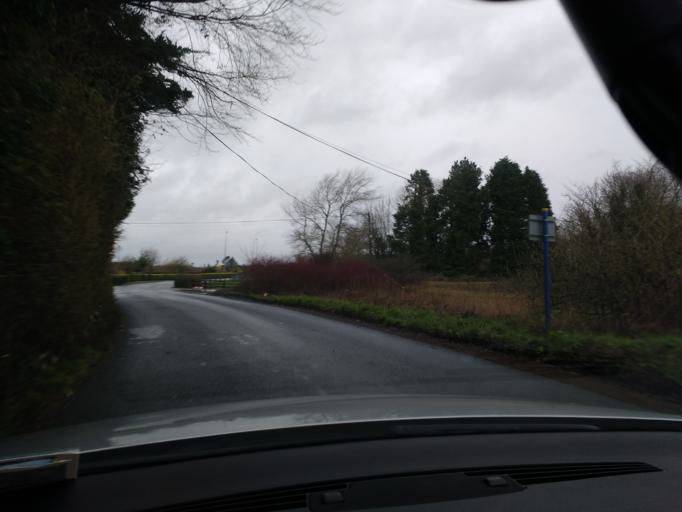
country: IE
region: Leinster
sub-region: Laois
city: Rathdowney
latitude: 52.6949
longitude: -7.6305
